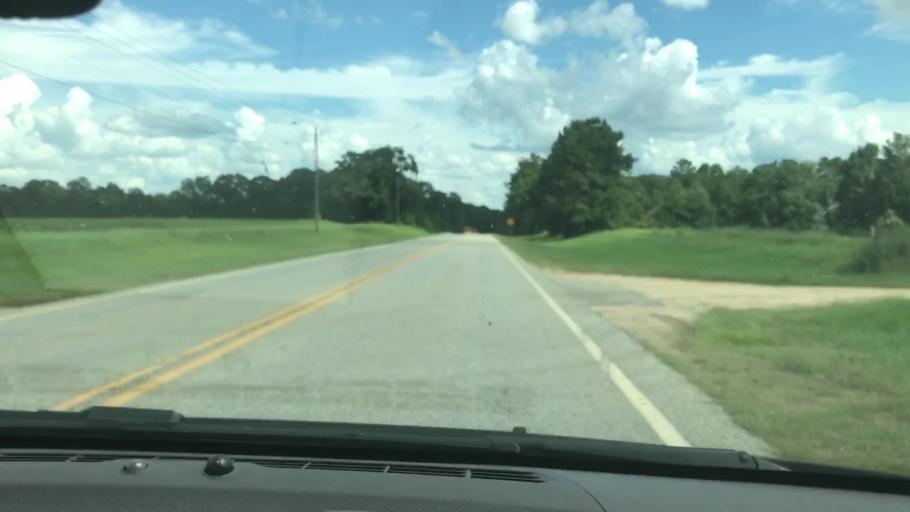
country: US
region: Georgia
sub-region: Quitman County
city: Georgetown
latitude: 31.7555
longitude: -85.0617
